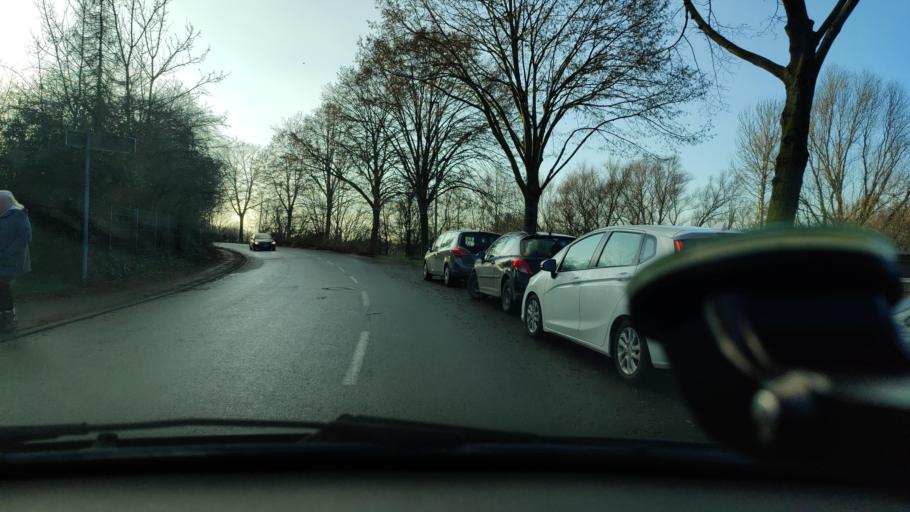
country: DE
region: North Rhine-Westphalia
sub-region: Regierungsbezirk Dusseldorf
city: Dinslaken
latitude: 51.5326
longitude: 6.7049
